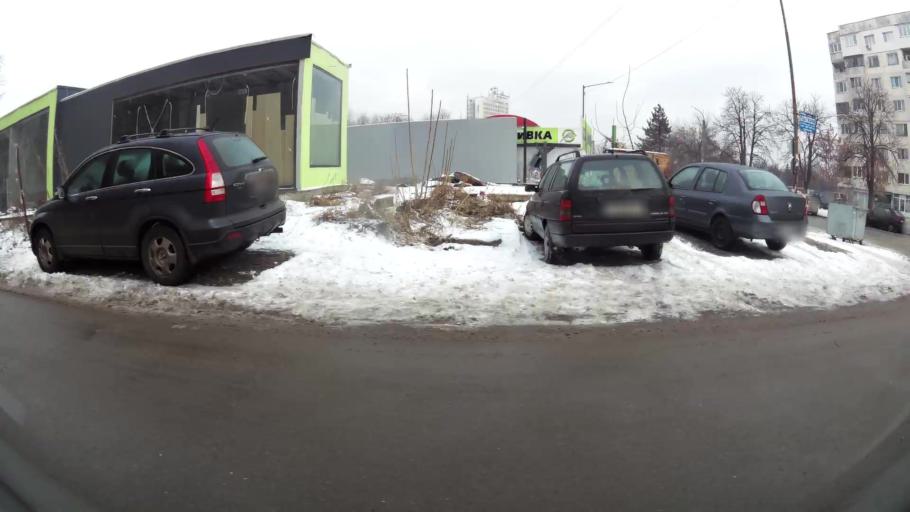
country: BG
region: Sofia-Capital
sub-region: Stolichna Obshtina
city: Sofia
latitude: 42.7144
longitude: 23.2979
